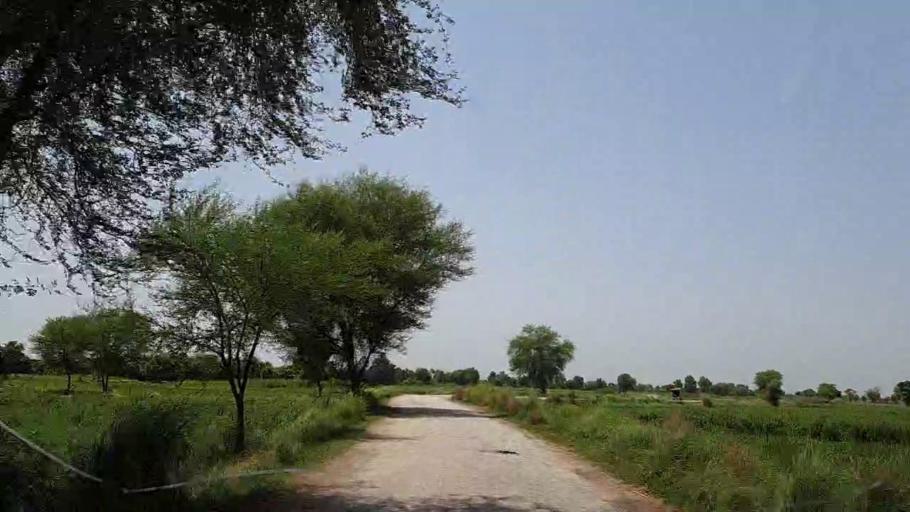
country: PK
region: Sindh
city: Tharu Shah
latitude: 26.9279
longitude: 68.0528
